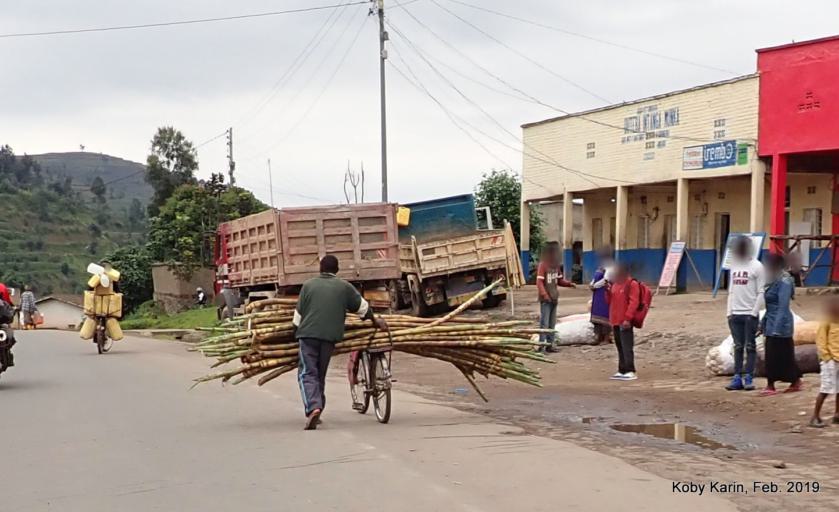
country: RW
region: Northern Province
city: Musanze
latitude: -1.6114
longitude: 29.4516
